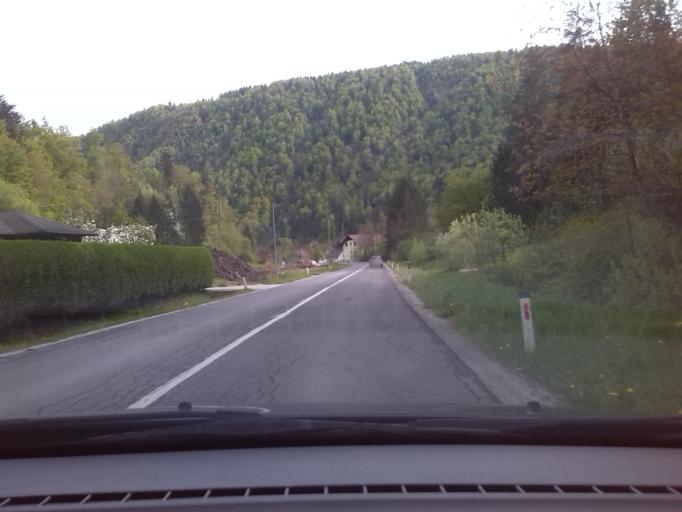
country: SI
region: Kamnik
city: Mekinje
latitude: 46.2313
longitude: 14.6672
